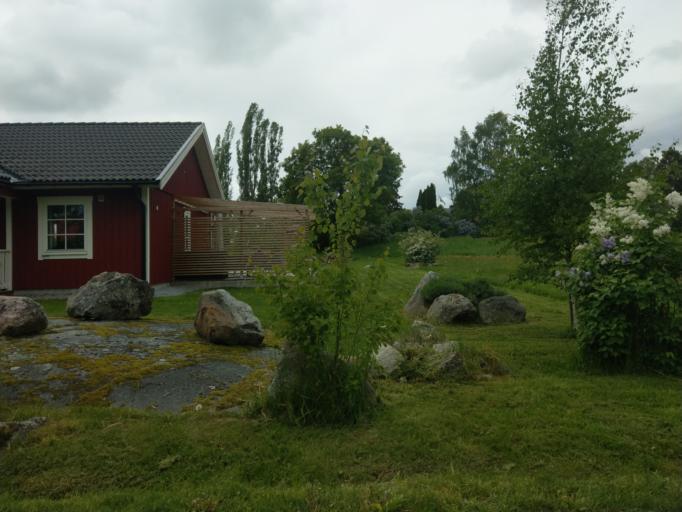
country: SE
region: Stockholm
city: Stenhamra
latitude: 59.4064
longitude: 17.6286
